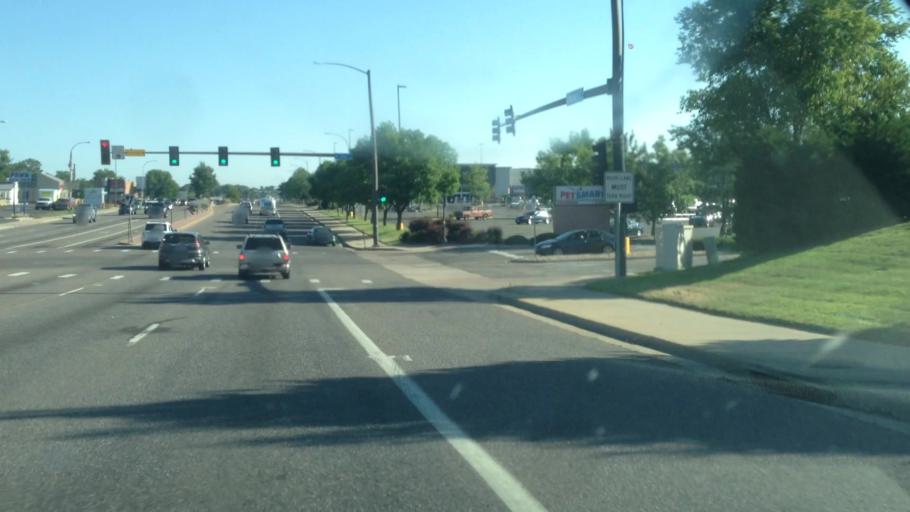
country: US
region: Colorado
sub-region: Jefferson County
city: Lakewood
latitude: 39.7198
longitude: -105.0814
